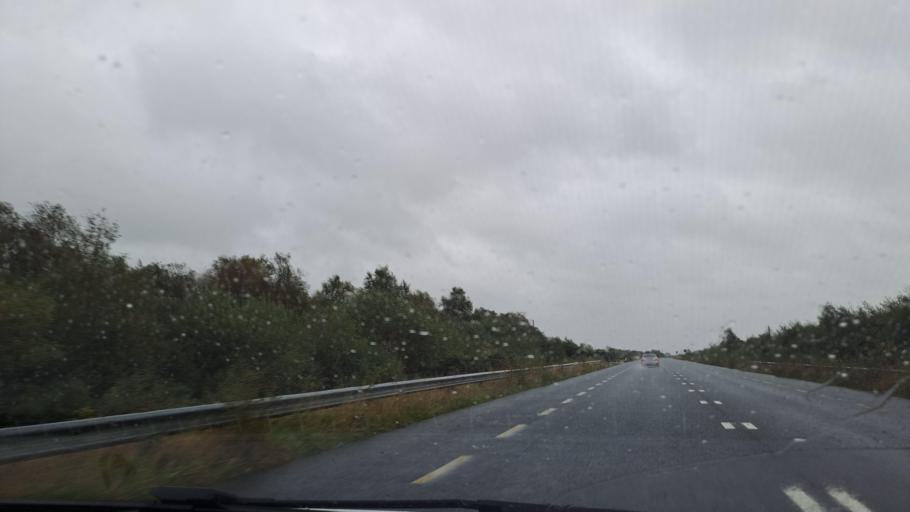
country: IE
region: Ulster
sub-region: County Monaghan
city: Carrickmacross
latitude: 53.9732
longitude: -6.6180
